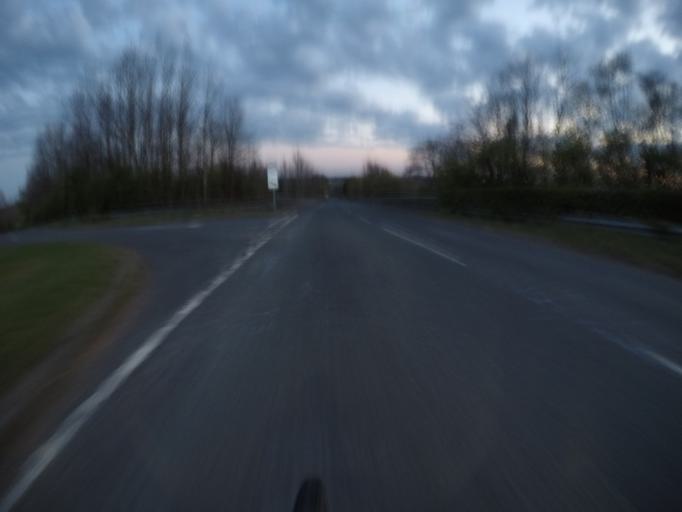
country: GB
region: Scotland
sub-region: South Ayrshire
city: Dundonald
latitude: 55.5518
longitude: -4.6199
